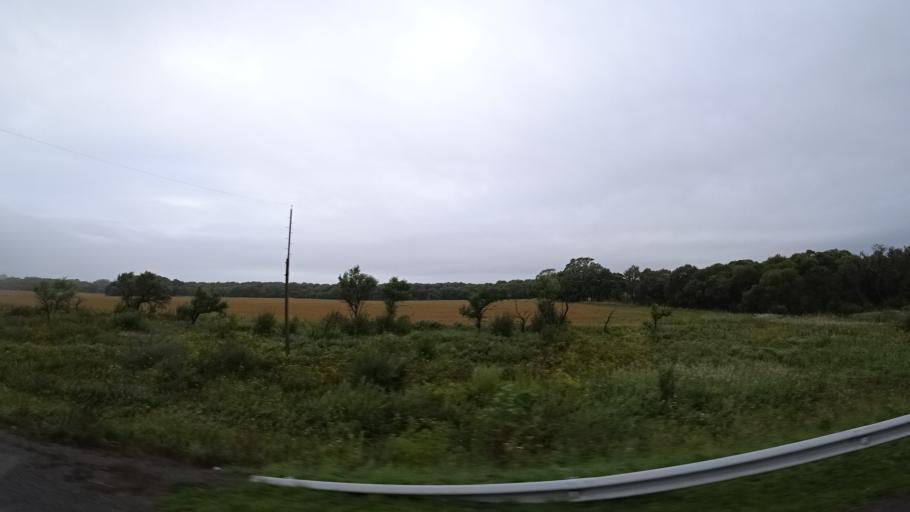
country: RU
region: Primorskiy
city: Monastyrishche
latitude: 44.2821
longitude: 132.4941
